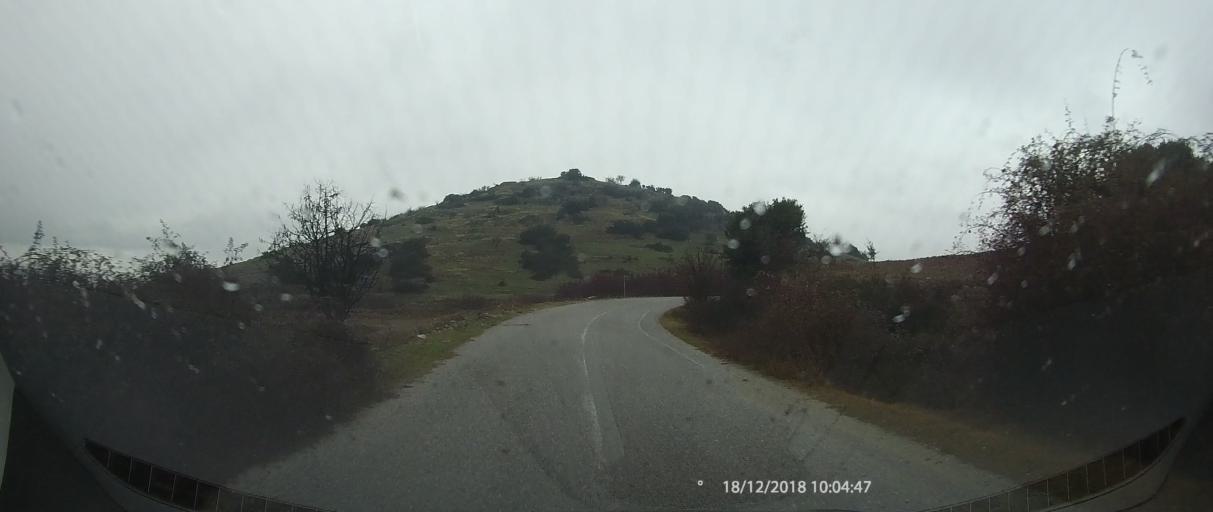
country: GR
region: Thessaly
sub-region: Nomos Larisis
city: Livadi
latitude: 40.0558
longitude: 22.2219
